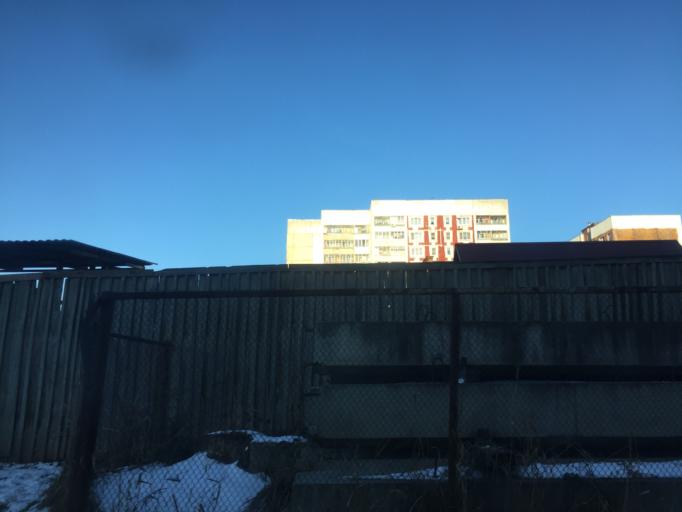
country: RU
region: Tula
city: Tula
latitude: 54.2142
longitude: 37.5994
